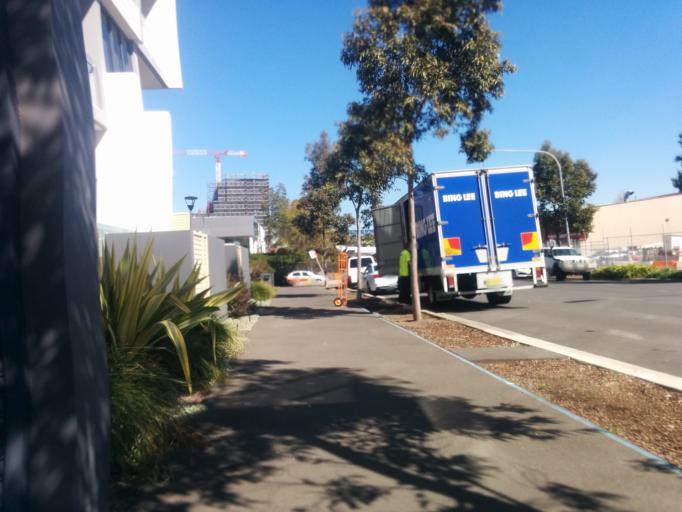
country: AU
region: New South Wales
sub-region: City of Sydney
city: Alexandria
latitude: -33.9092
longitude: 151.2115
